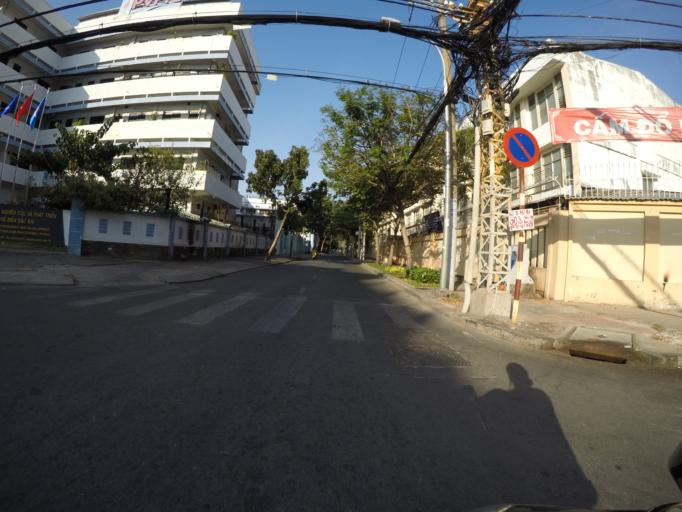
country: VN
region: Ho Chi Minh City
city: Quan Ba
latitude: 10.7769
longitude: 106.6861
